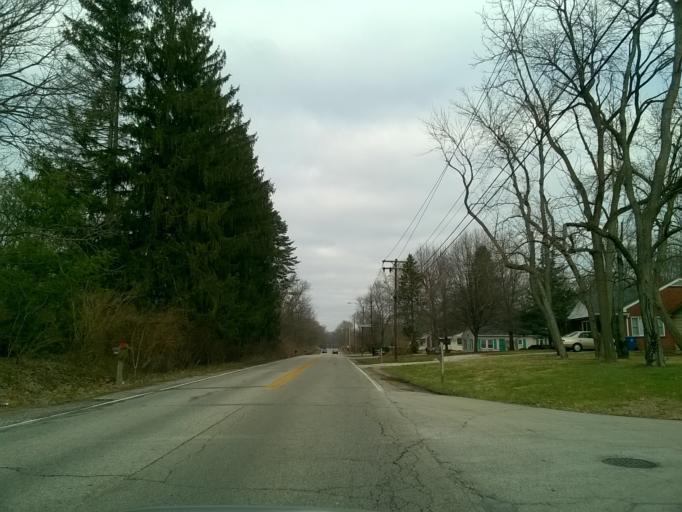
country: US
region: Indiana
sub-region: Marion County
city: Broad Ripple
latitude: 39.8836
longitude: -86.1387
